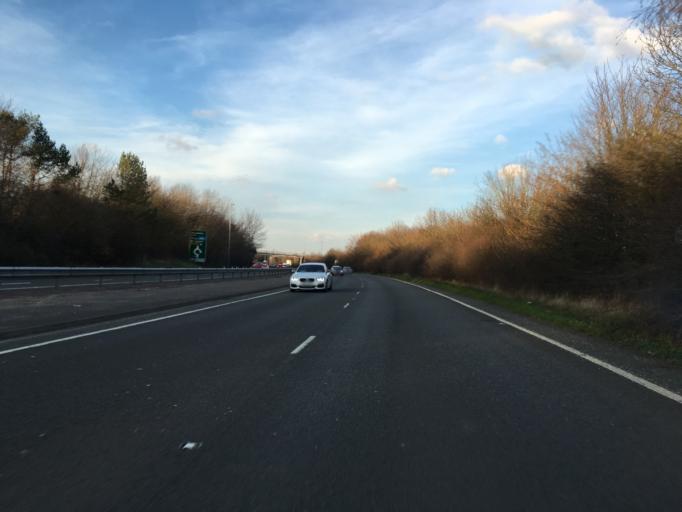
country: GB
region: England
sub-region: Borough of Stockport
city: Cheadle Hulme
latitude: 53.3451
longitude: -2.1996
